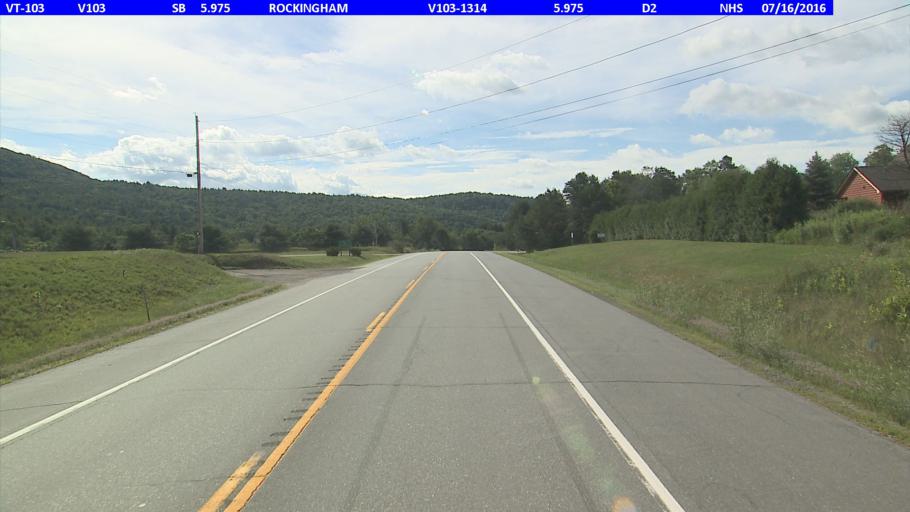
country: US
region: Vermont
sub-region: Windsor County
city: Chester
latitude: 43.2270
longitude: -72.5429
